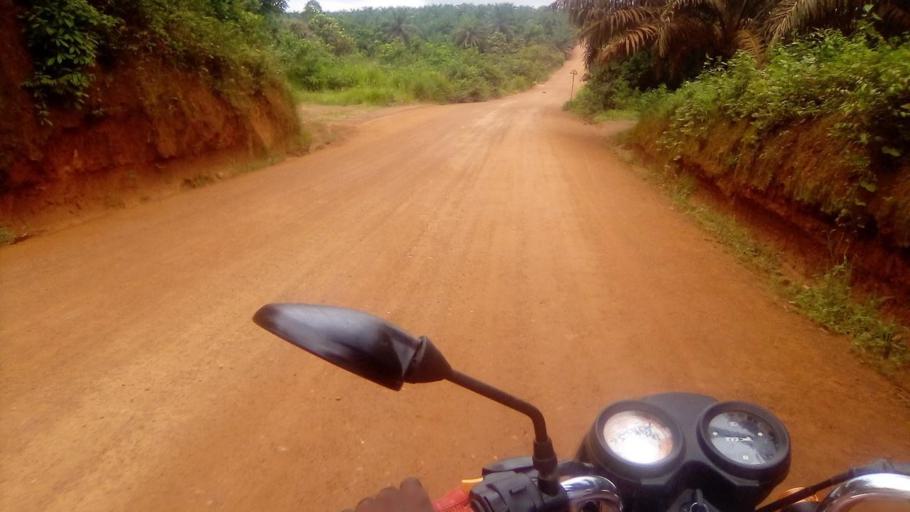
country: SL
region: Southern Province
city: Tongole
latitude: 7.4323
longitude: -11.8532
